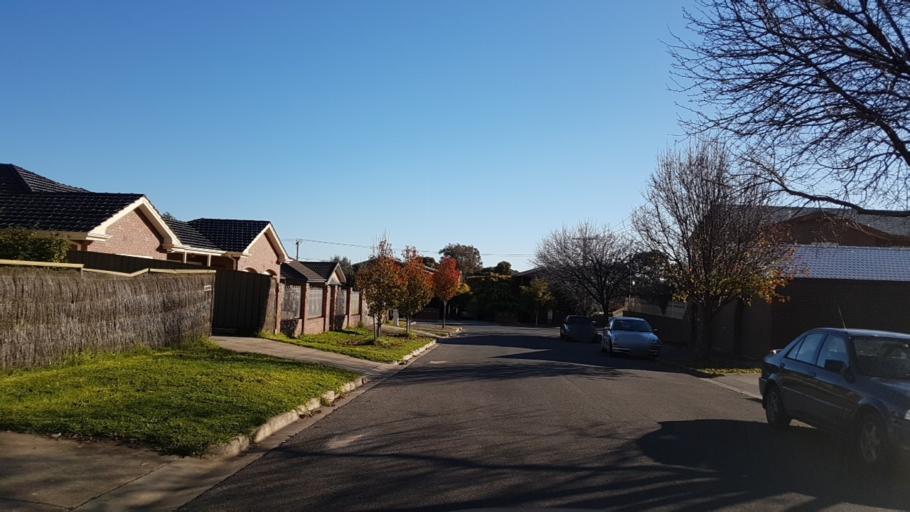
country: AU
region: South Australia
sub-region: Campbelltown
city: Paradise
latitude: -34.8783
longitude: 138.6798
